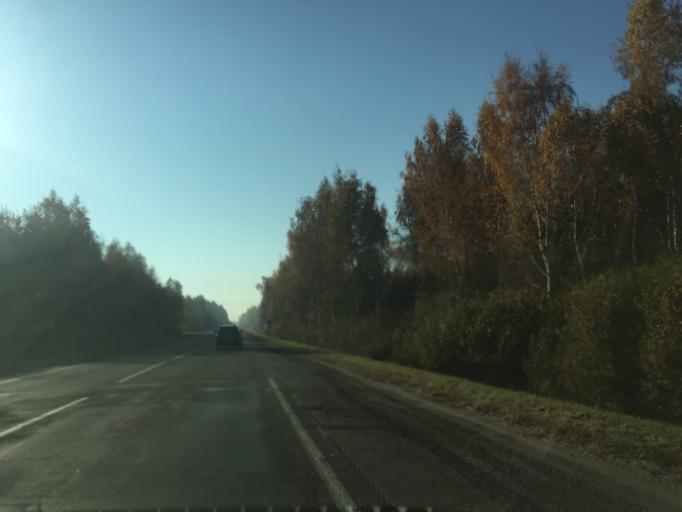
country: BY
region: Gomel
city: Kastsyukowka
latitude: 52.4380
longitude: 30.8260
